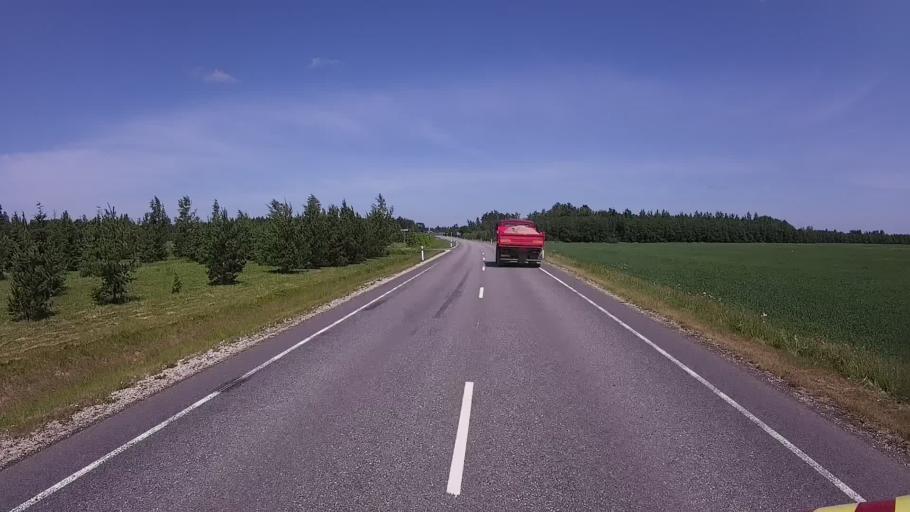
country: EE
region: Tartu
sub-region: Tartu linn
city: Tartu
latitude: 58.3988
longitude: 26.8960
